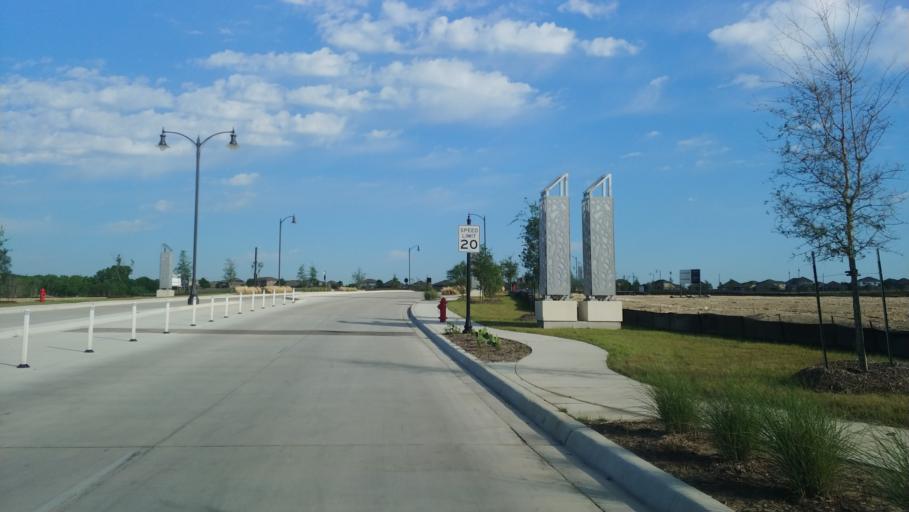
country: US
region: Texas
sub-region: Bexar County
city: Live Oak
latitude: 29.5632
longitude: -98.3413
